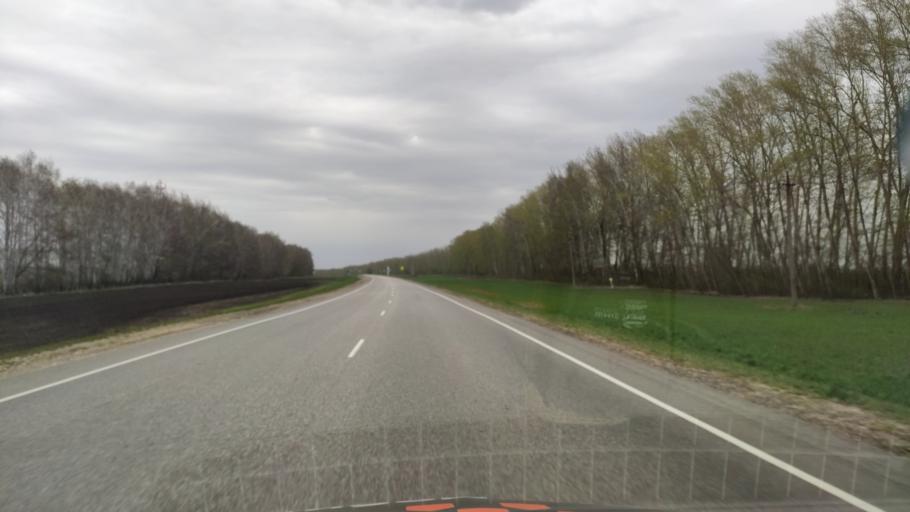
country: RU
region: Kursk
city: Olym
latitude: 51.5503
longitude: 38.1962
